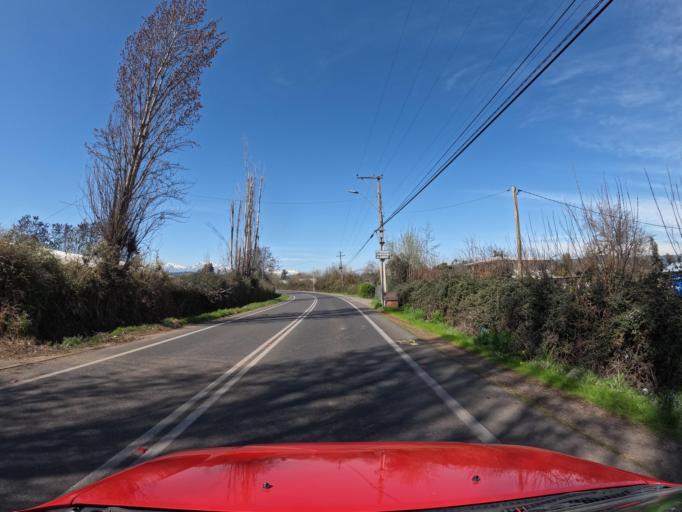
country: CL
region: Maule
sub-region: Provincia de Curico
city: Teno
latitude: -34.9694
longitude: -71.0226
